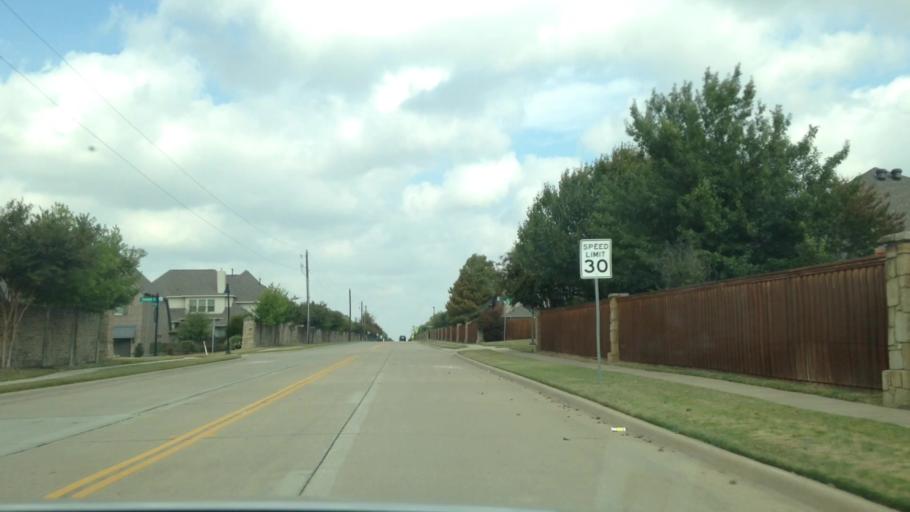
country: US
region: Texas
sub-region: Collin County
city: Allen
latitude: 33.1170
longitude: -96.7070
